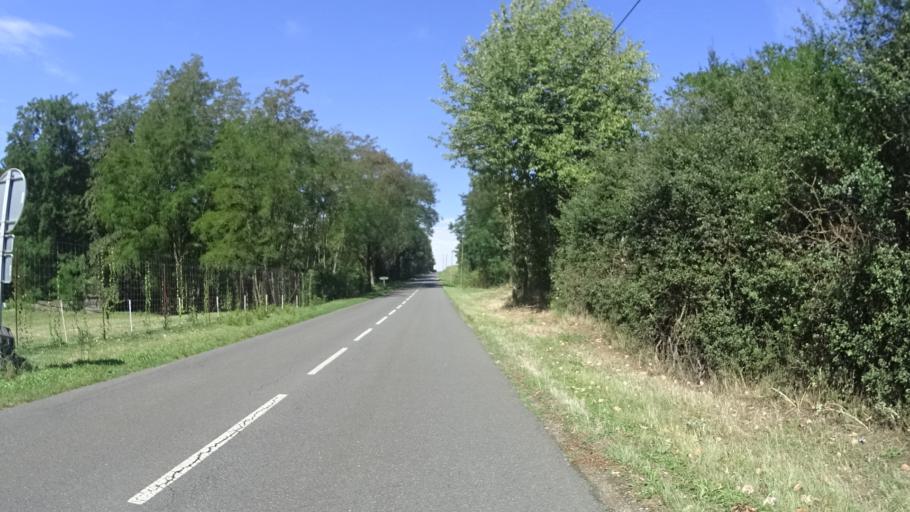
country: FR
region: Centre
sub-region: Departement du Loiret
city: Briare
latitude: 47.6029
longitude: 2.7651
